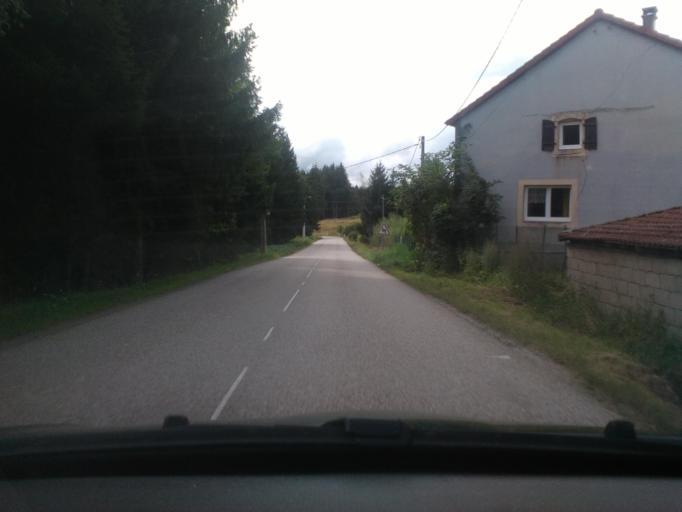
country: FR
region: Lorraine
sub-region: Departement des Vosges
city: Corcieux
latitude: 48.1458
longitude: 6.8517
